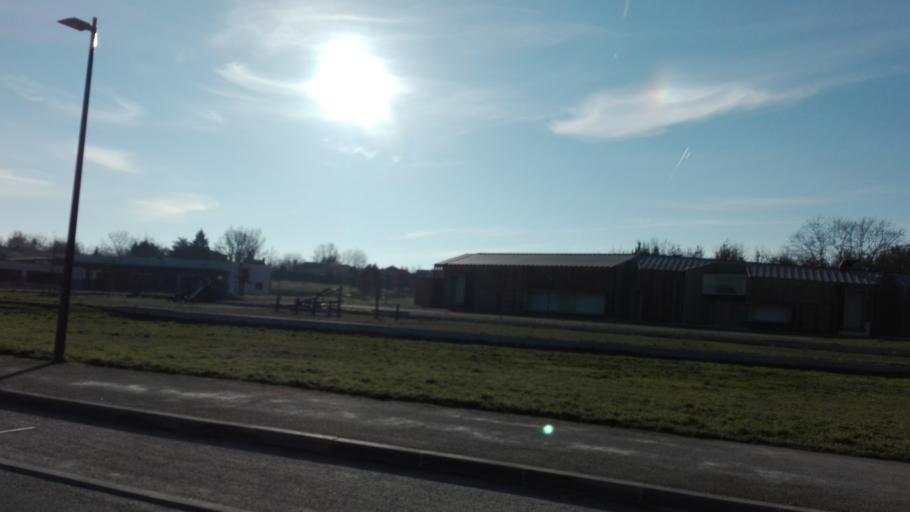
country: FR
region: Midi-Pyrenees
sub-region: Departement de la Haute-Garonne
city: Grenade
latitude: 43.7625
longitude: 1.2965
